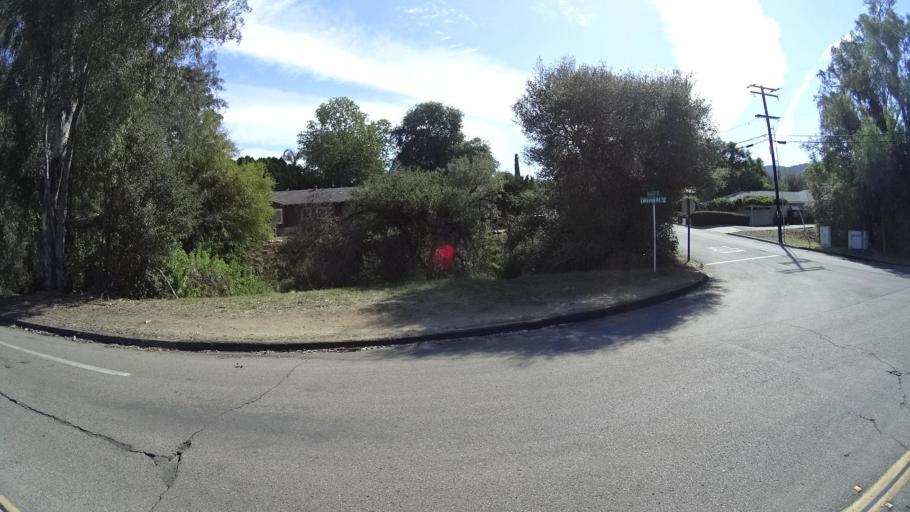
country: US
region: California
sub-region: San Diego County
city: Lakeside
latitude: 32.8400
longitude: -116.9050
